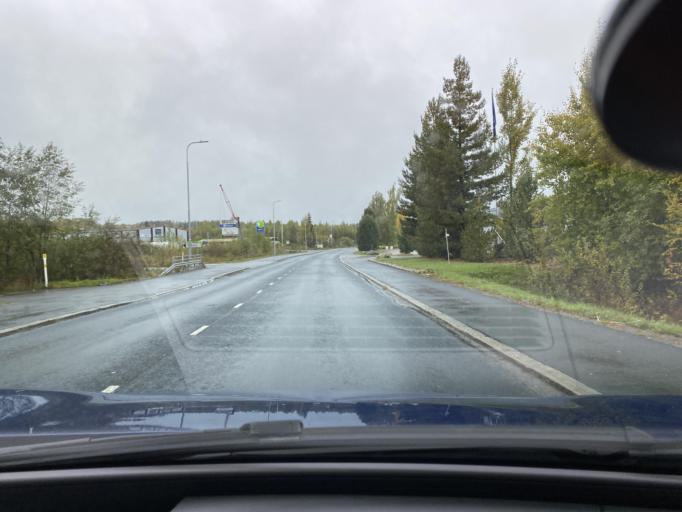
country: FI
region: Pirkanmaa
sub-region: Tampere
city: Tampere
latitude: 61.4562
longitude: 23.7357
